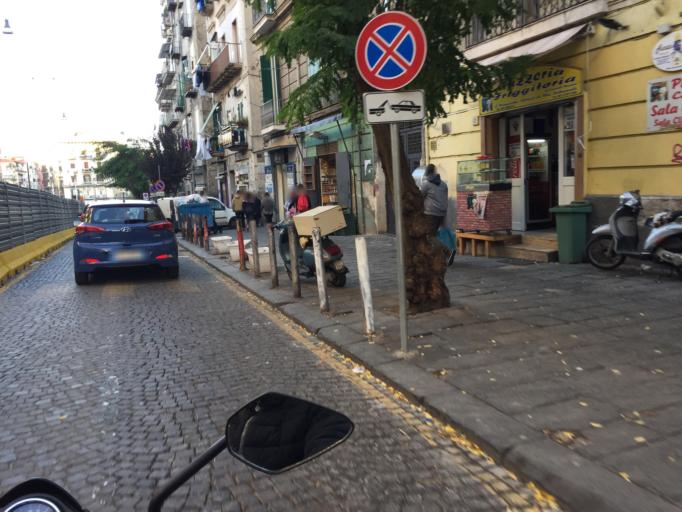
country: IT
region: Campania
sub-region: Provincia di Napoli
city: Napoli
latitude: 40.8546
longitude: 14.2630
